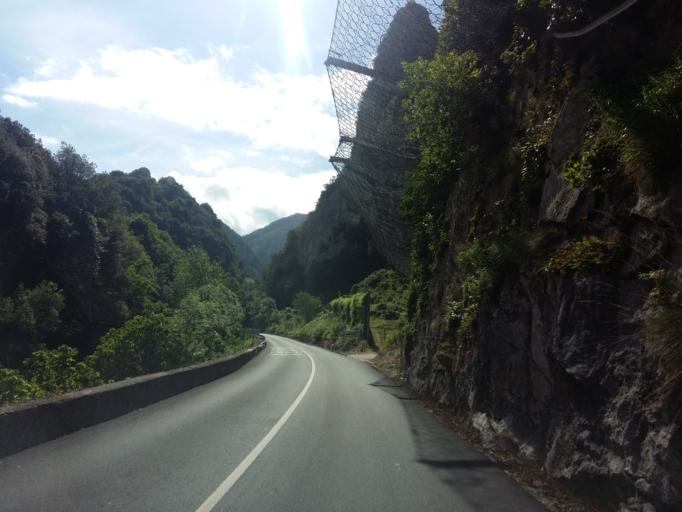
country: ES
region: Cantabria
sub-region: Provincia de Cantabria
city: Tresviso
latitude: 43.2516
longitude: -4.6067
